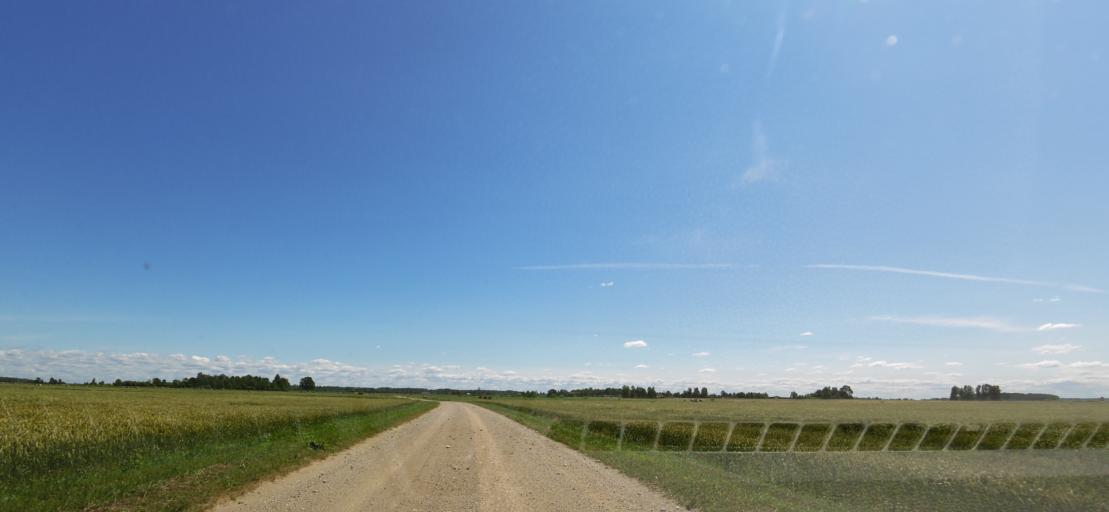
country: LT
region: Panevezys
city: Pasvalys
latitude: 56.2609
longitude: 24.5211
